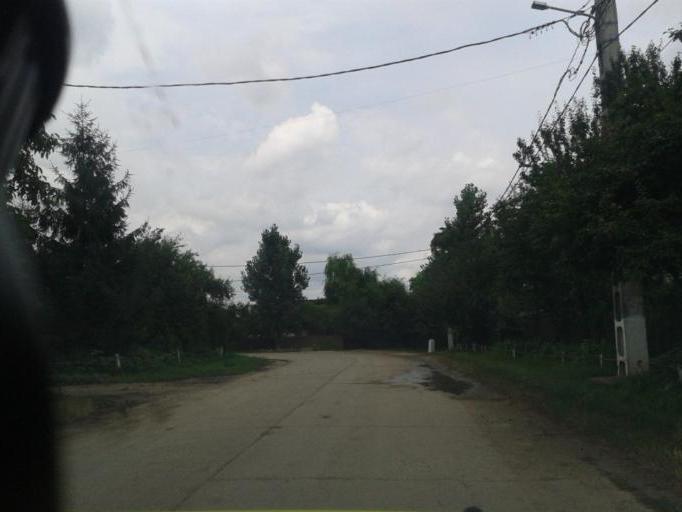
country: RO
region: Ialomita
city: Dragoesti-Snagov
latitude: 44.5306
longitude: 26.4832
